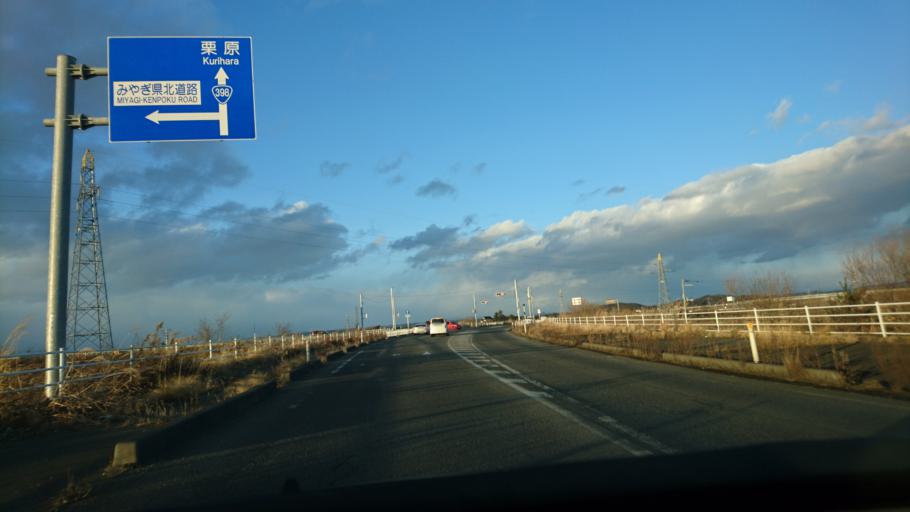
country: JP
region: Miyagi
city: Wakuya
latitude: 38.7264
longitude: 141.1484
